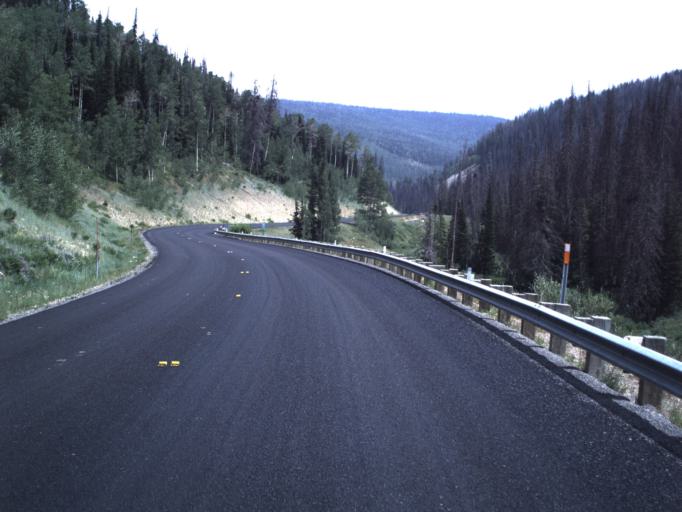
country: US
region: Utah
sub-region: Summit County
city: Francis
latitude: 40.4902
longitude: -110.9940
